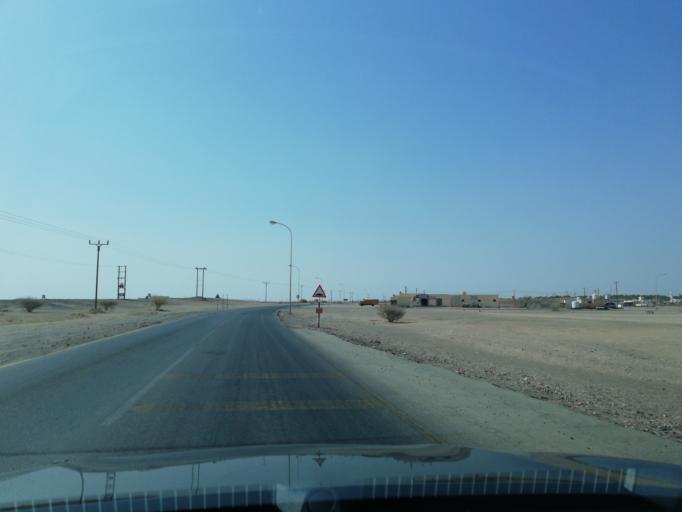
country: OM
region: Muhafazat ad Dakhiliyah
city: Adam
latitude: 22.3105
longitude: 58.0696
